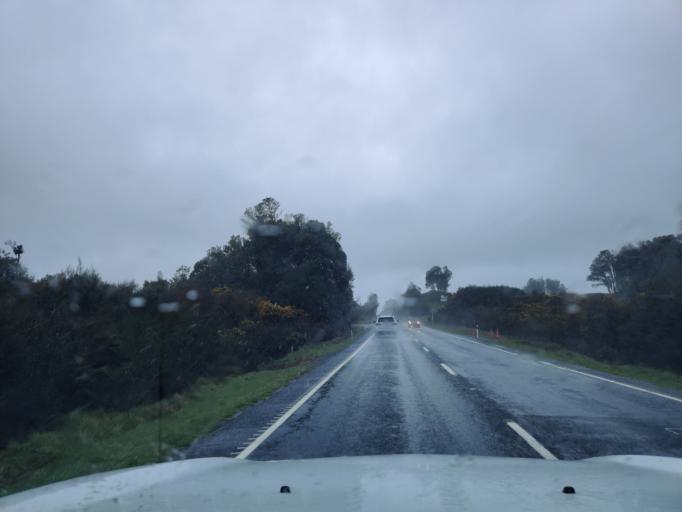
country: NZ
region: Bay of Plenty
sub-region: Rotorua District
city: Rotorua
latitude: -38.0393
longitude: 176.0537
